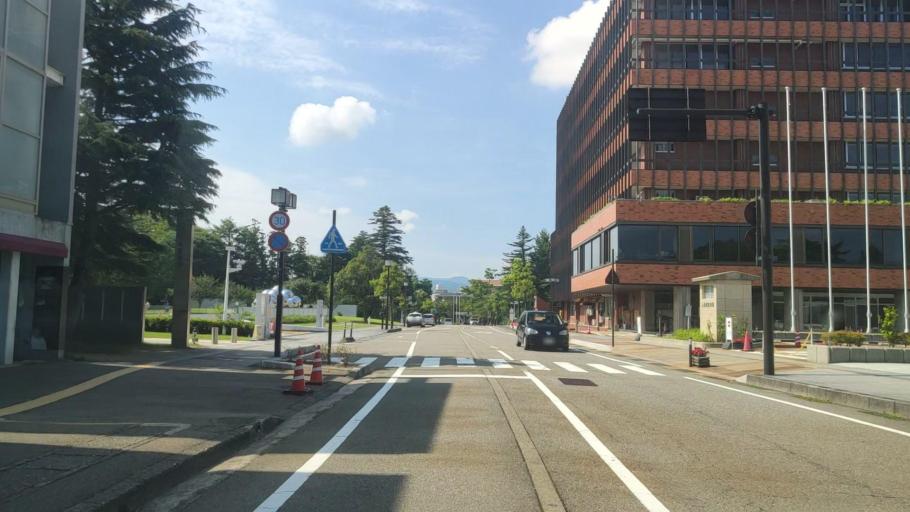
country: JP
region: Ishikawa
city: Kanazawa-shi
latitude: 36.5615
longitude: 136.6571
